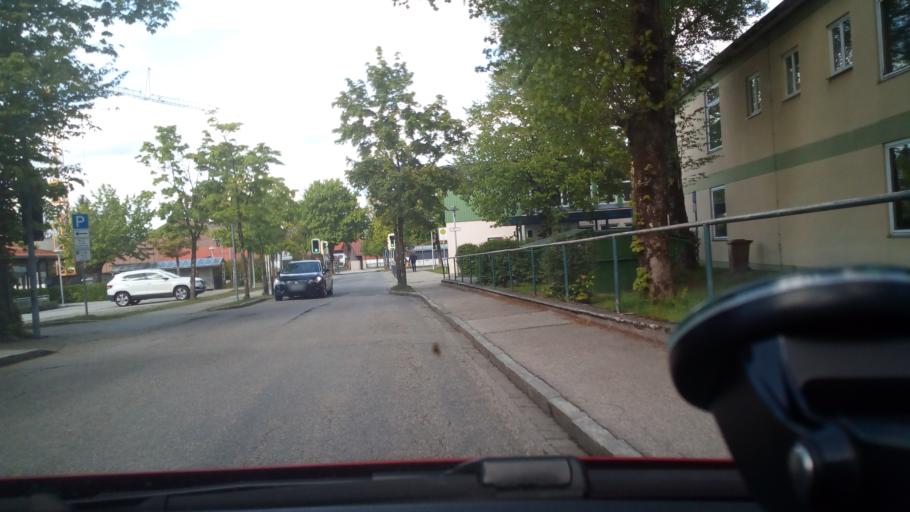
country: DE
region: Bavaria
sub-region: Upper Bavaria
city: Holzkirchen
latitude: 47.8760
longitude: 11.6968
